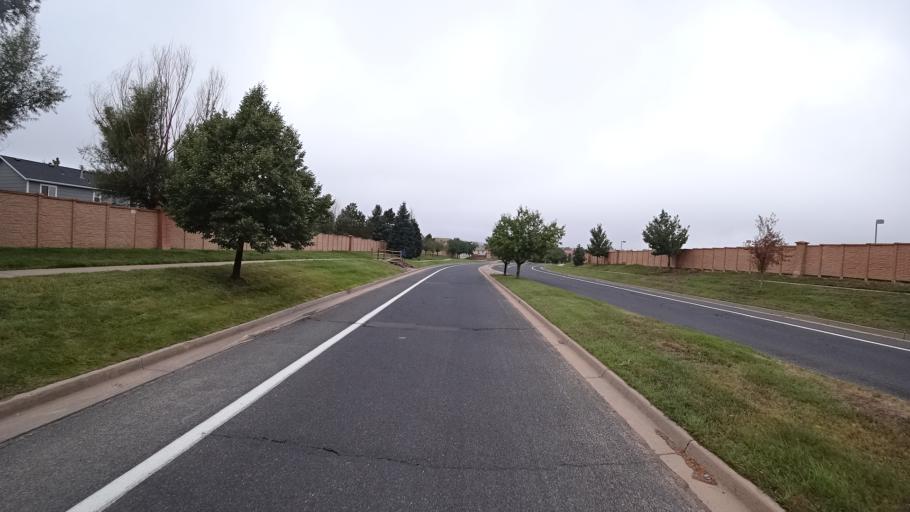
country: US
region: Colorado
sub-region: El Paso County
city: Black Forest
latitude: 38.9359
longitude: -104.7360
